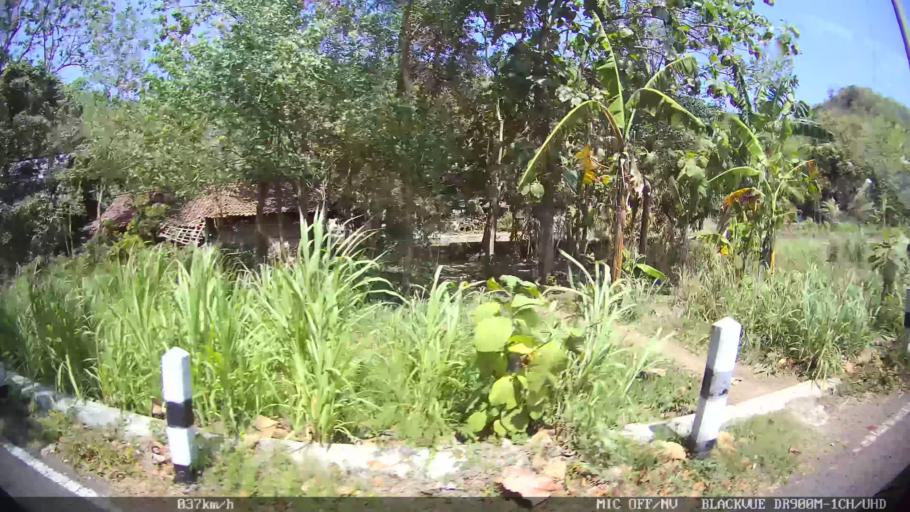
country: ID
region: Daerah Istimewa Yogyakarta
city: Pundong
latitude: -7.9578
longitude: 110.3636
